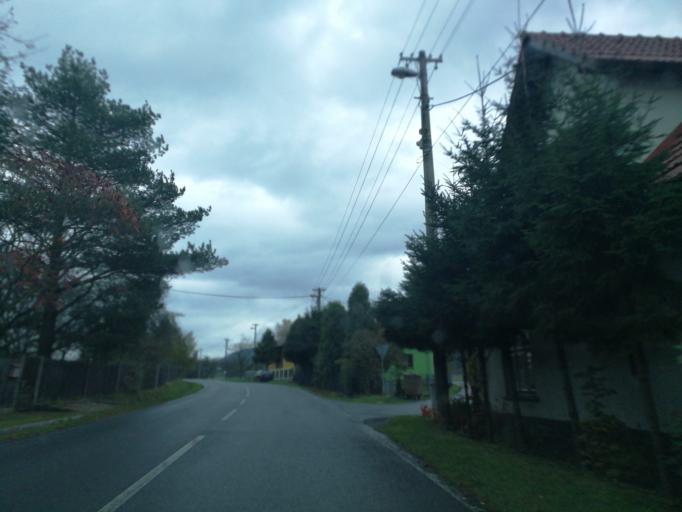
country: CZ
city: Hodslavice
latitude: 49.5364
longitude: 18.0327
